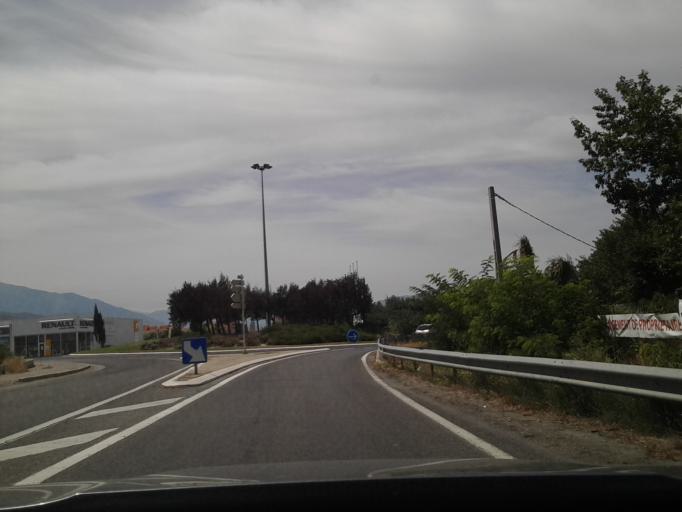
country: FR
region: Languedoc-Roussillon
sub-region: Departement des Pyrenees-Orientales
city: Ille-sur-Tet
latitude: 42.6780
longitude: 2.6337
